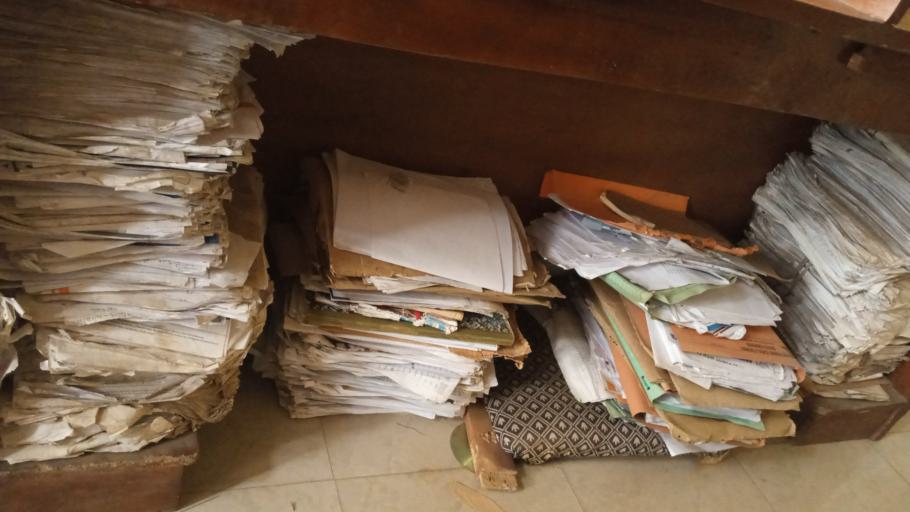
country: NG
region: Oyo
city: Ibadan
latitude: 7.4088
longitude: 3.9037
